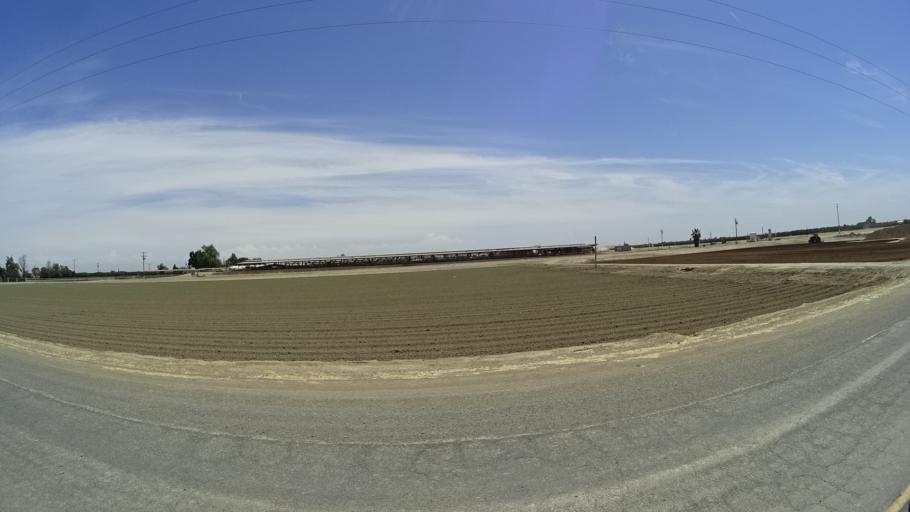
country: US
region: California
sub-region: Kings County
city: Armona
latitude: 36.3403
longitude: -119.7270
